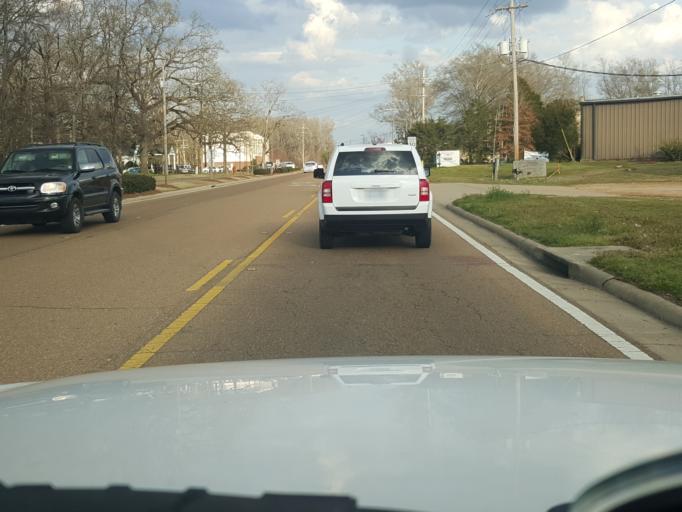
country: US
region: Mississippi
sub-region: Rankin County
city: Flowood
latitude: 32.3417
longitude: -90.0758
